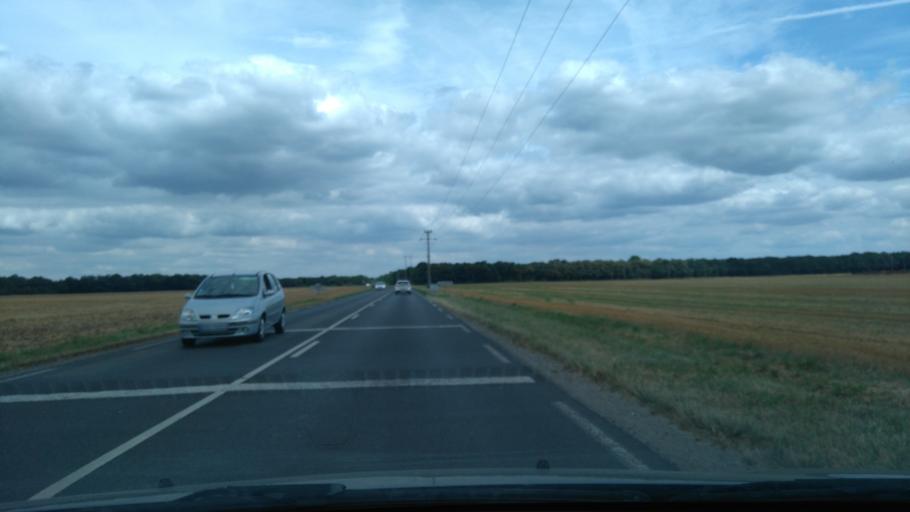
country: FR
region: Picardie
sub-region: Departement de l'Oise
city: Gouvieux
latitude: 49.2012
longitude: 2.4360
